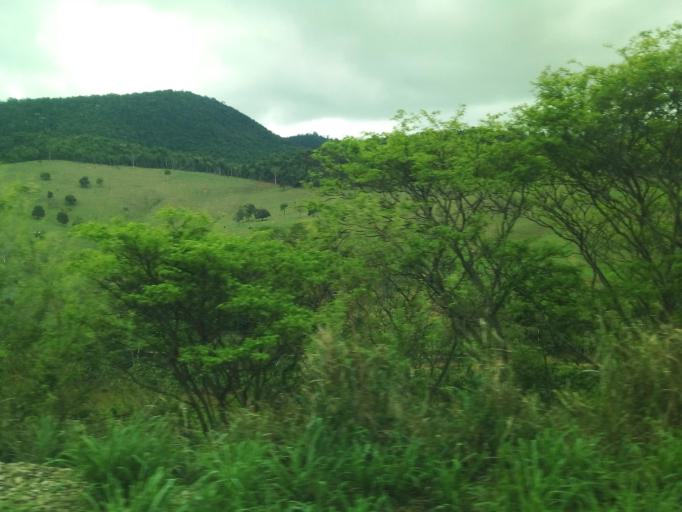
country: BR
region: Minas Gerais
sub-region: Nova Era
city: Nova Era
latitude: -19.6681
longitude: -42.8956
